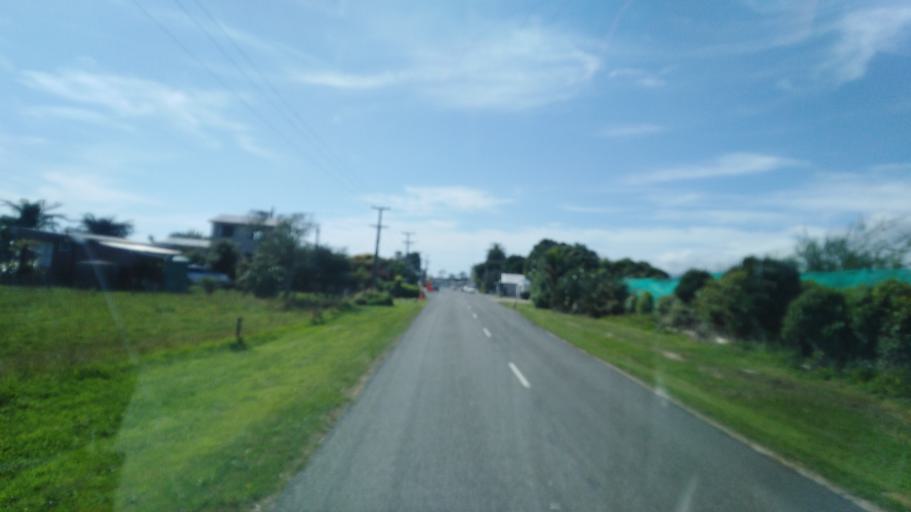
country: NZ
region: West Coast
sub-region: Buller District
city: Westport
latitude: -41.2534
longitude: 172.1295
